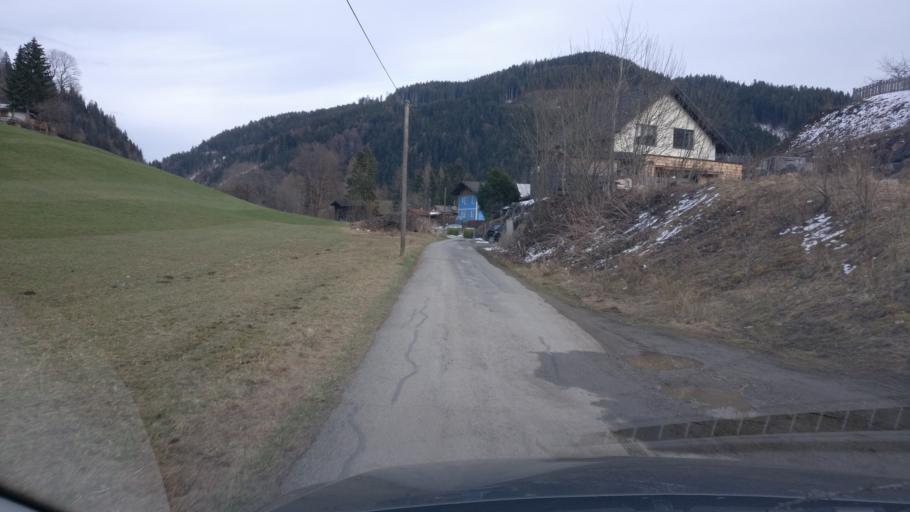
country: AT
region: Salzburg
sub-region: Politischer Bezirk Zell am See
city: Lend
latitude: 47.3147
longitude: 13.0329
